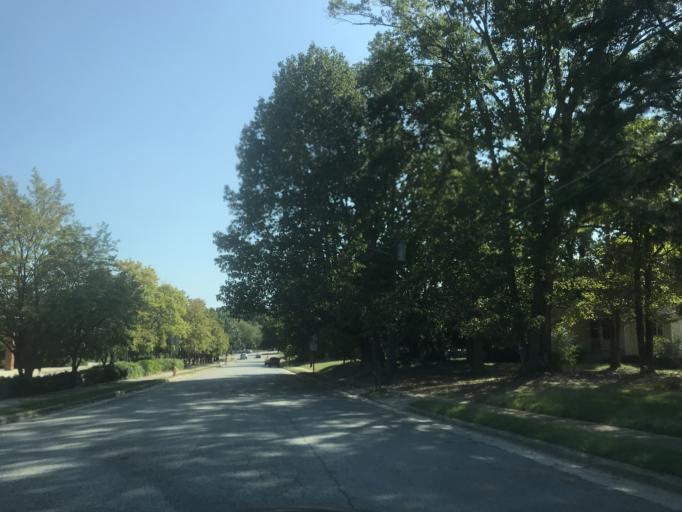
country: US
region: North Carolina
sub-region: Wake County
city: Raleigh
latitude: 35.7623
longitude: -78.6286
